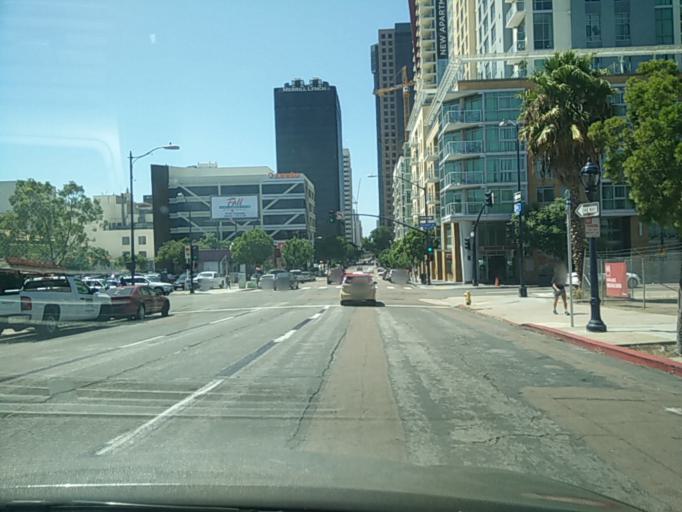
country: US
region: California
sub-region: San Diego County
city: San Diego
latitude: 32.7179
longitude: -117.1543
